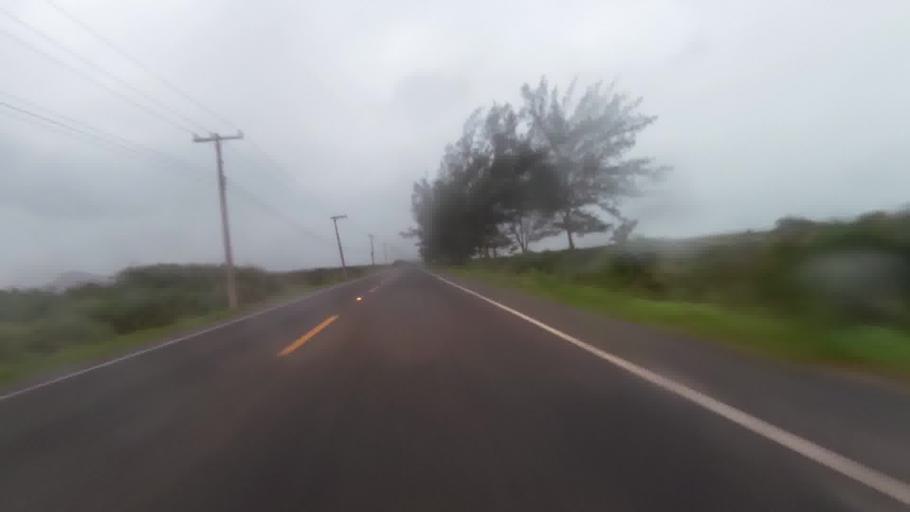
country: BR
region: Espirito Santo
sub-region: Itapemirim
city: Itapemirim
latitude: -20.9403
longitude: -40.8036
